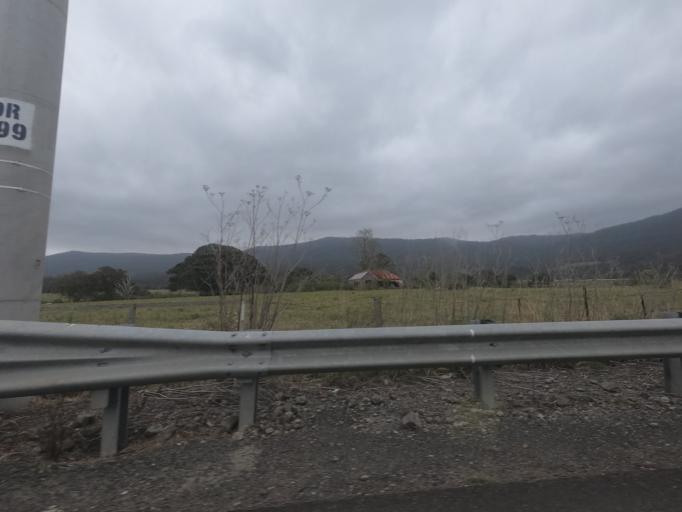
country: AU
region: New South Wales
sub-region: Wollongong
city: Dapto
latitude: -34.4702
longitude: 150.7948
